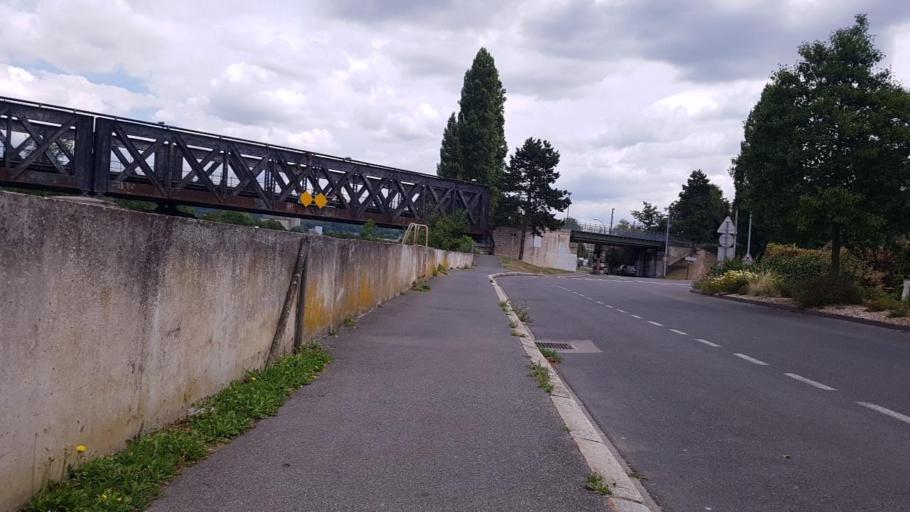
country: FR
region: Picardie
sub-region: Departement de l'Oise
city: Compiegne
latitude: 49.4266
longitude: 2.8349
